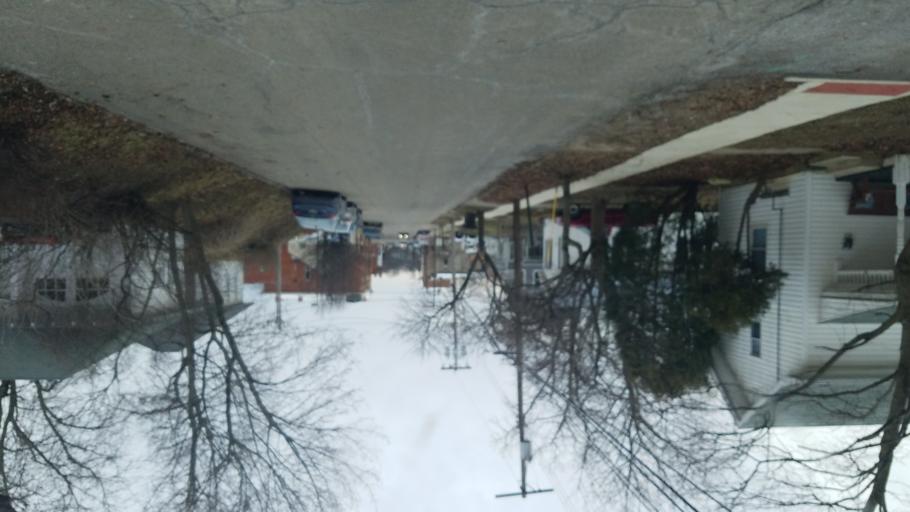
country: US
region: Ohio
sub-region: Morrow County
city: Mount Gilead
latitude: 40.5483
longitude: -82.8262
